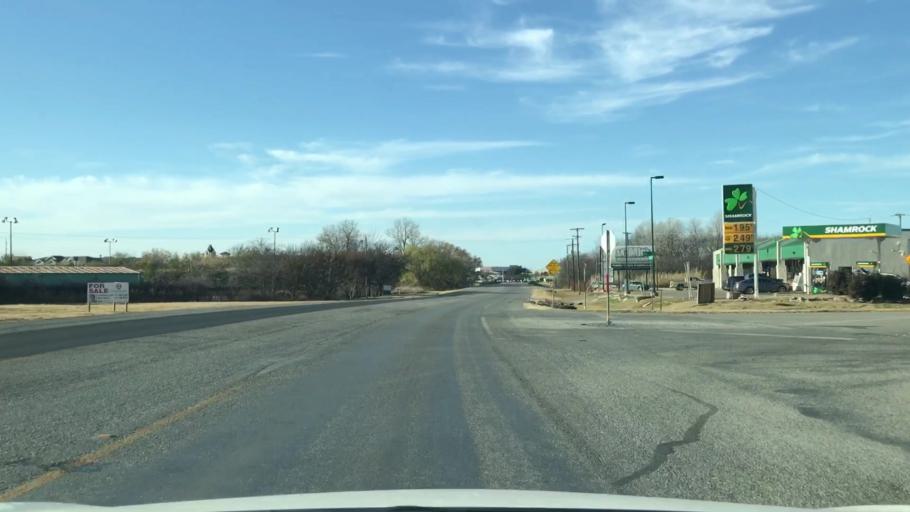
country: US
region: Texas
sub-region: Johnson County
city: Burleson
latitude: 32.5400
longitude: -97.3079
